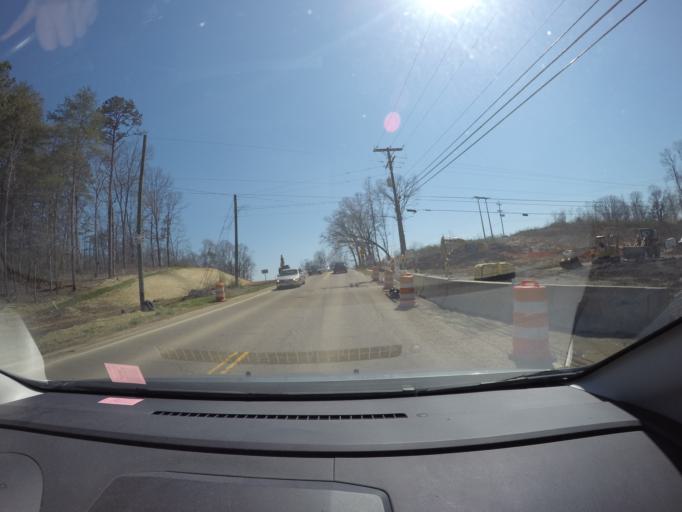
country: US
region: Tennessee
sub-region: Hamilton County
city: Collegedale
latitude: 35.0685
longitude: -85.0975
